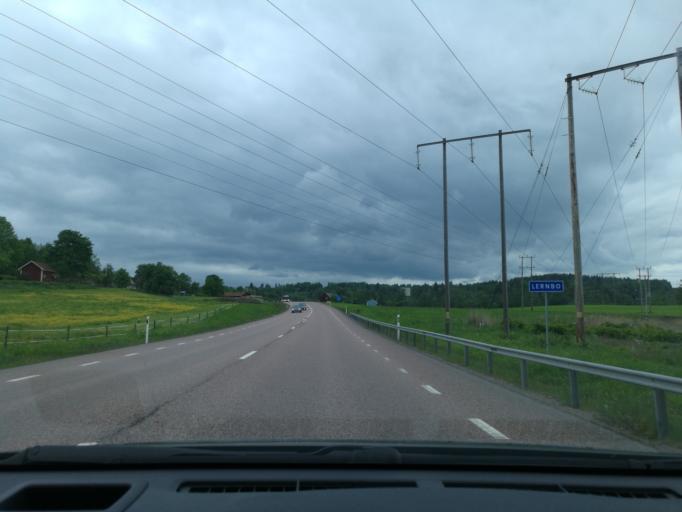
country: SE
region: Dalarna
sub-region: Smedjebackens Kommun
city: Smedjebacken
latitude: 60.1409
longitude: 15.3276
